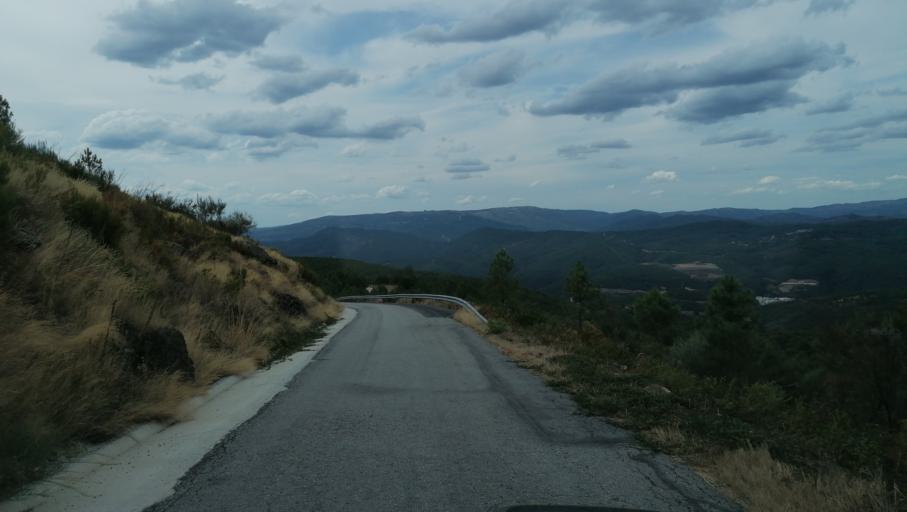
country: PT
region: Vila Real
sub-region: Vila Pouca de Aguiar
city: Vila Pouca de Aguiar
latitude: 41.5562
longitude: -7.7025
